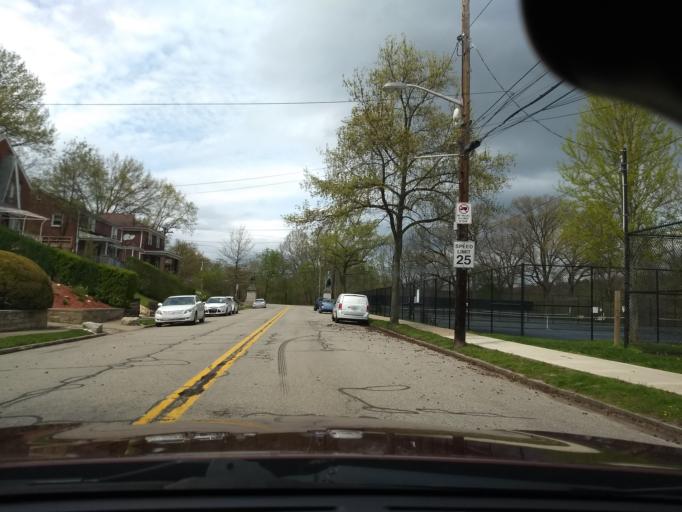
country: US
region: Pennsylvania
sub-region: Allegheny County
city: Aspinwall
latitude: 40.4743
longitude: -79.9109
